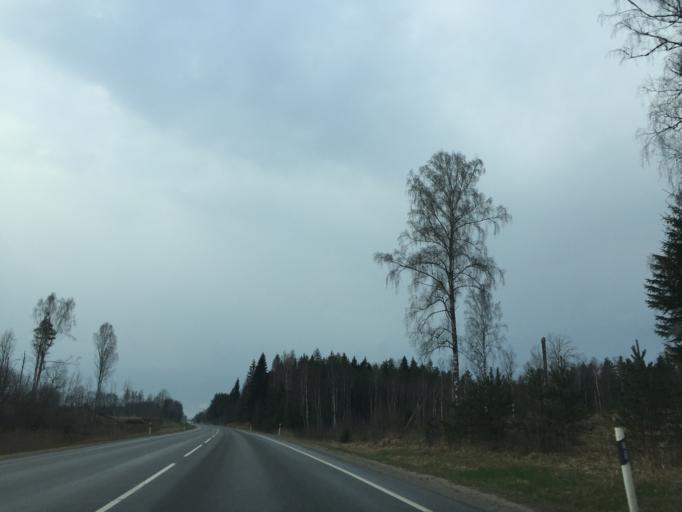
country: EE
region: Tartu
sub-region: UElenurme vald
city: Ulenurme
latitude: 58.1287
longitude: 26.7269
